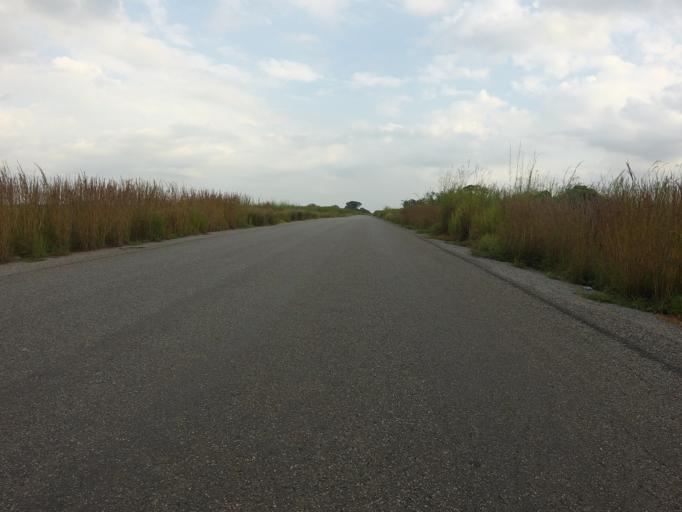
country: GH
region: Volta
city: Ho
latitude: 6.4210
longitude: 0.5194
